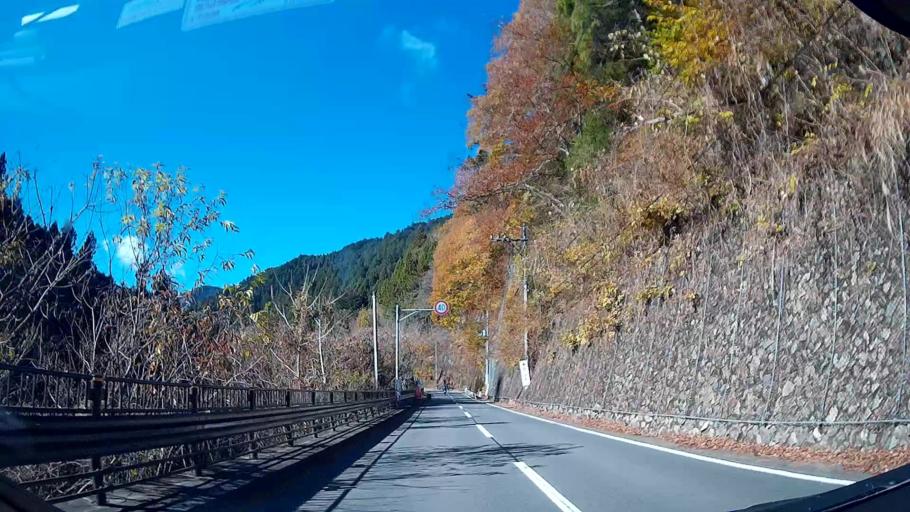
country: JP
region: Tokyo
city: Itsukaichi
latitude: 35.7063
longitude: 139.1491
